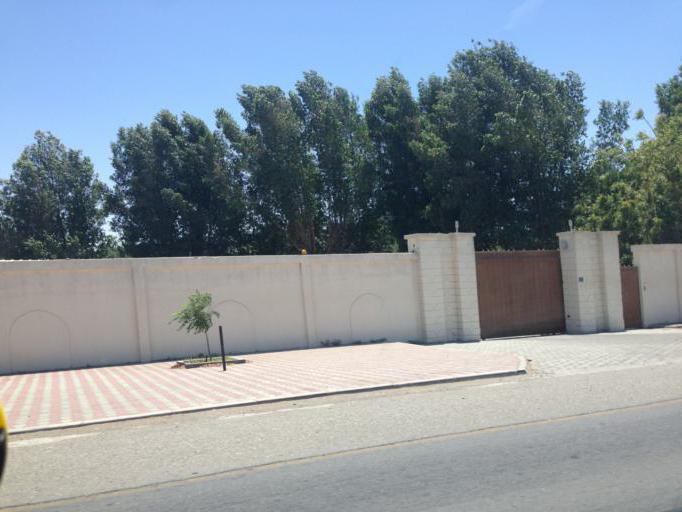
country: OM
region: Muhafazat Masqat
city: As Sib al Jadidah
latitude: 23.6637
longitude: 58.2067
